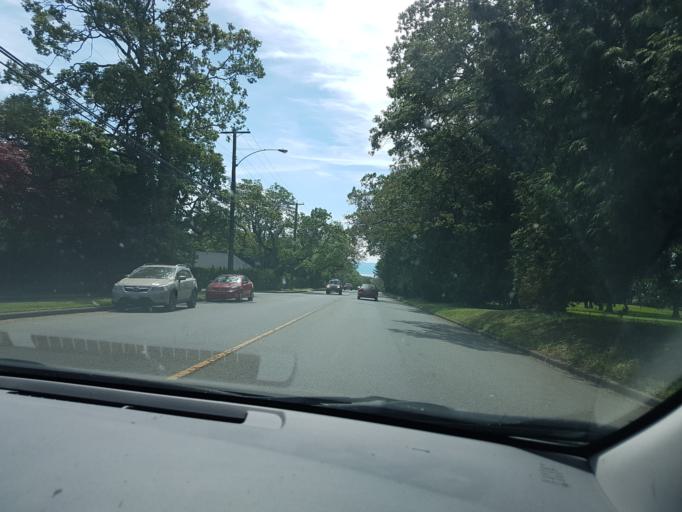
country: CA
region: British Columbia
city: Oak Bay
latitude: 48.4474
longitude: -123.3101
